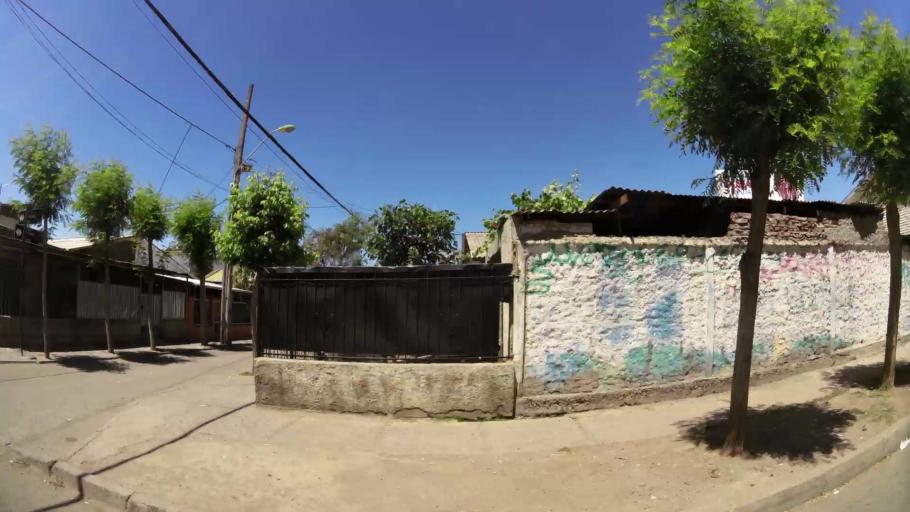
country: CL
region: Santiago Metropolitan
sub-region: Provincia de Santiago
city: La Pintana
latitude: -33.5719
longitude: -70.6631
